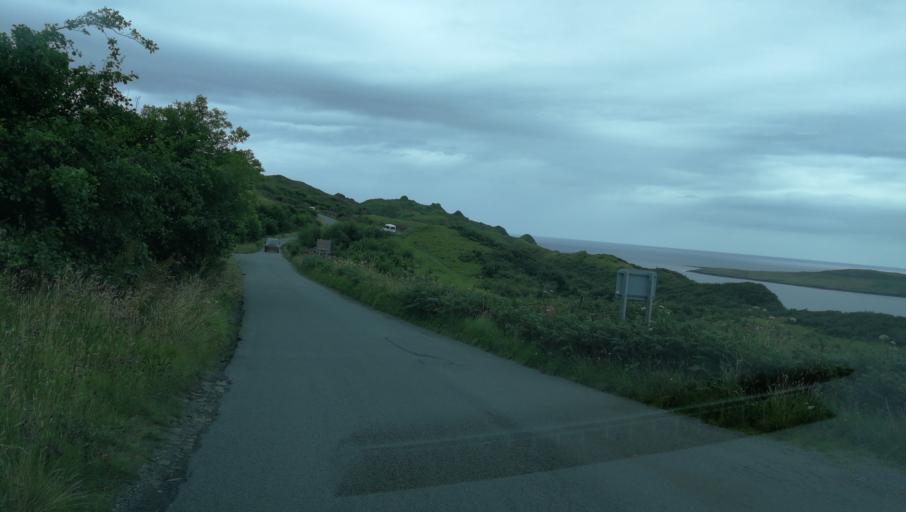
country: GB
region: Scotland
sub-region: Highland
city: Portree
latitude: 57.6449
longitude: -6.2423
